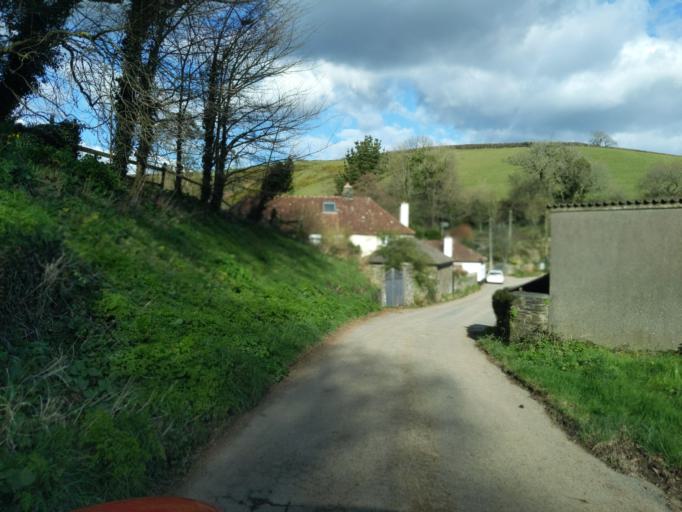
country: GB
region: England
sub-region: Devon
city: Kingsbridge
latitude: 50.2914
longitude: -3.7604
